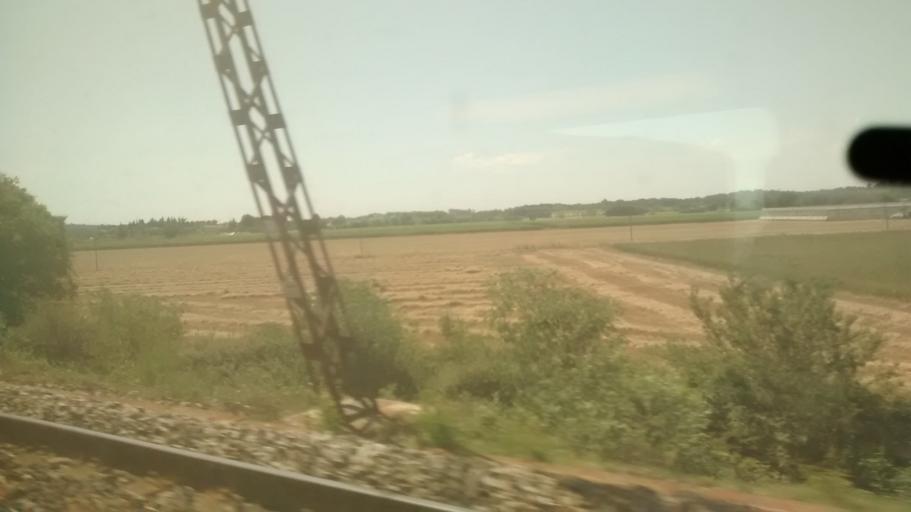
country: FR
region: Languedoc-Roussillon
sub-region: Departement de l'Herault
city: Lunel
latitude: 43.6943
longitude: 4.1505
